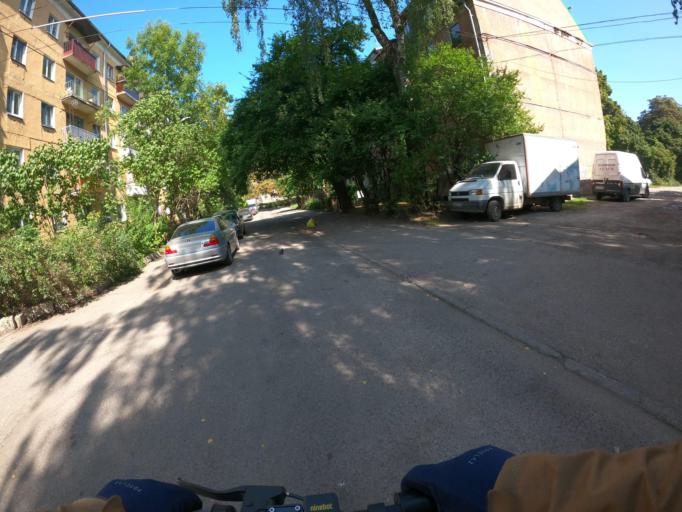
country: RU
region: Kaliningrad
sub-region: Gorod Kaliningrad
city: Kaliningrad
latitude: 54.7254
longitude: 20.5110
